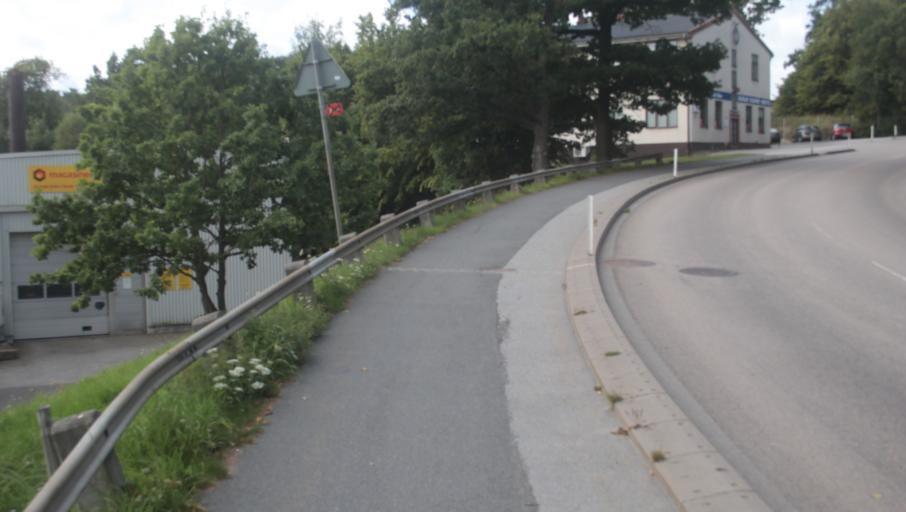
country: SE
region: Blekinge
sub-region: Karlshamns Kommun
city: Karlshamn
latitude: 56.1799
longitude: 14.8475
